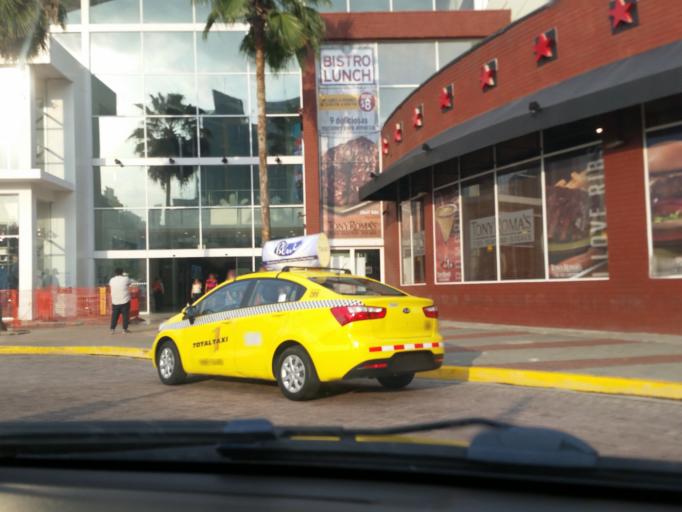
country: PA
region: Panama
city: Panama
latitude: 8.9853
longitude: -79.5119
